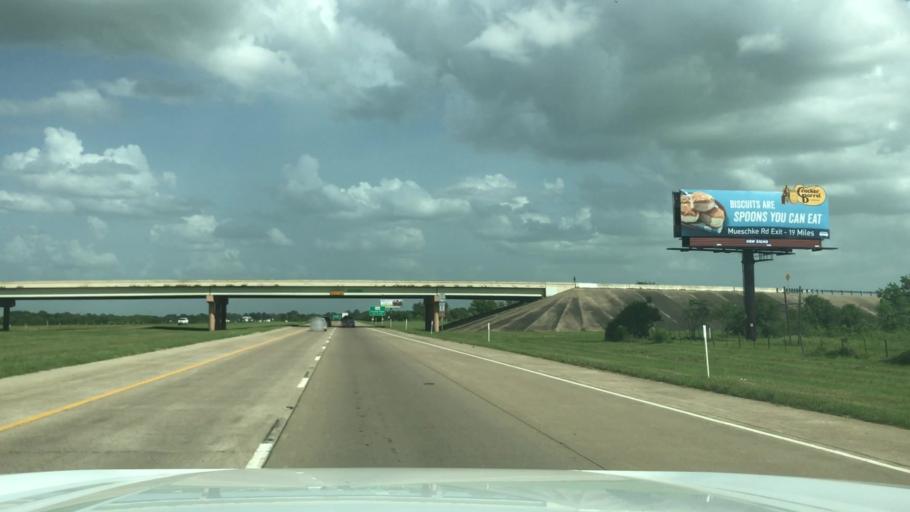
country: US
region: Texas
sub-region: Waller County
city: Prairie View
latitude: 30.0843
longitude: -96.0061
